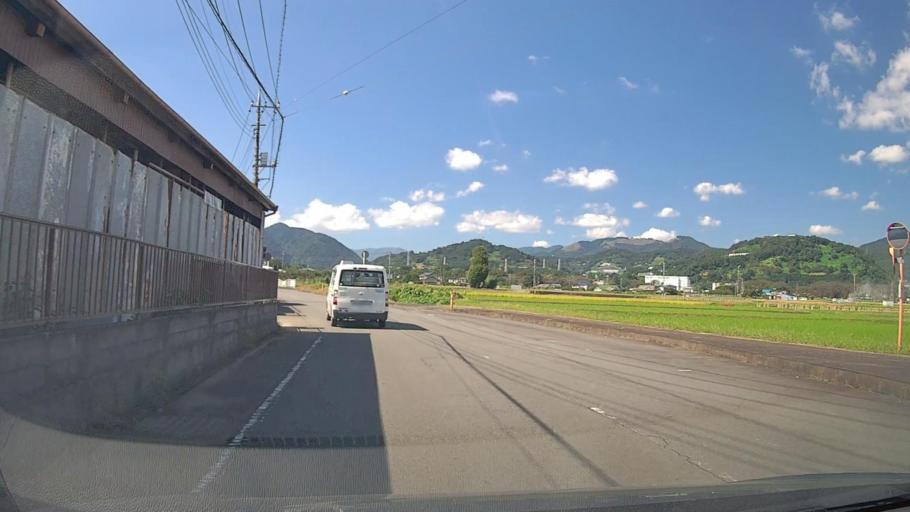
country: JP
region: Kanagawa
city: Odawara
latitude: 35.3461
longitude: 139.1078
